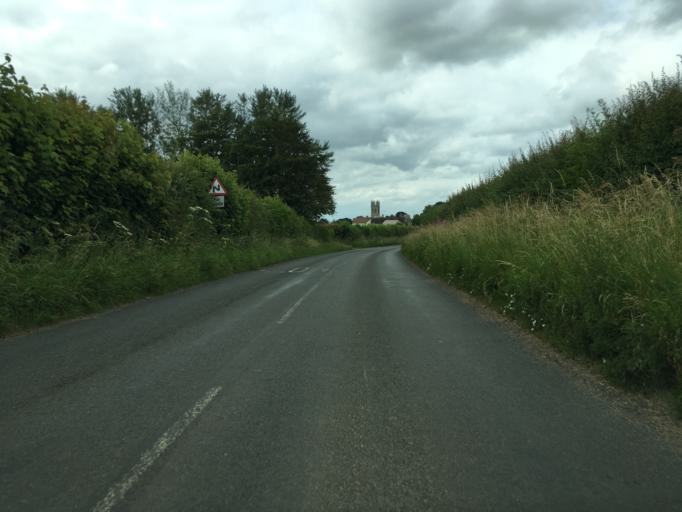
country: GB
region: England
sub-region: Oxfordshire
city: Chipping Norton
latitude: 51.9188
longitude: -1.5859
